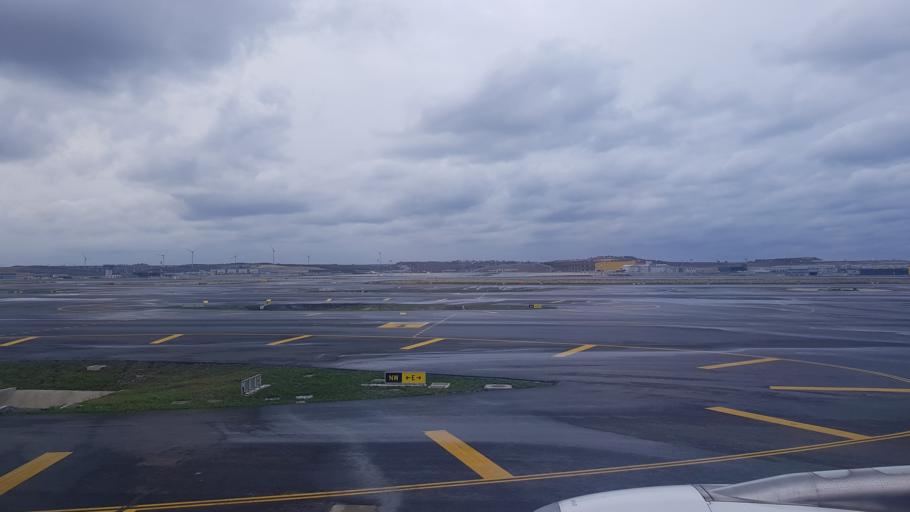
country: TR
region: Istanbul
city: Durusu
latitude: 41.2683
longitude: 28.7334
